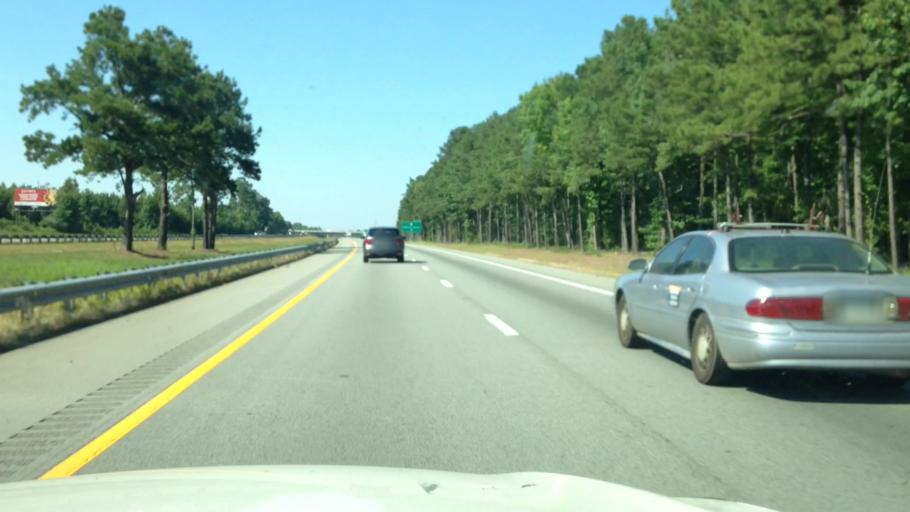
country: US
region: North Carolina
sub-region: Halifax County
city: Weldon
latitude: 36.3927
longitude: -77.6474
